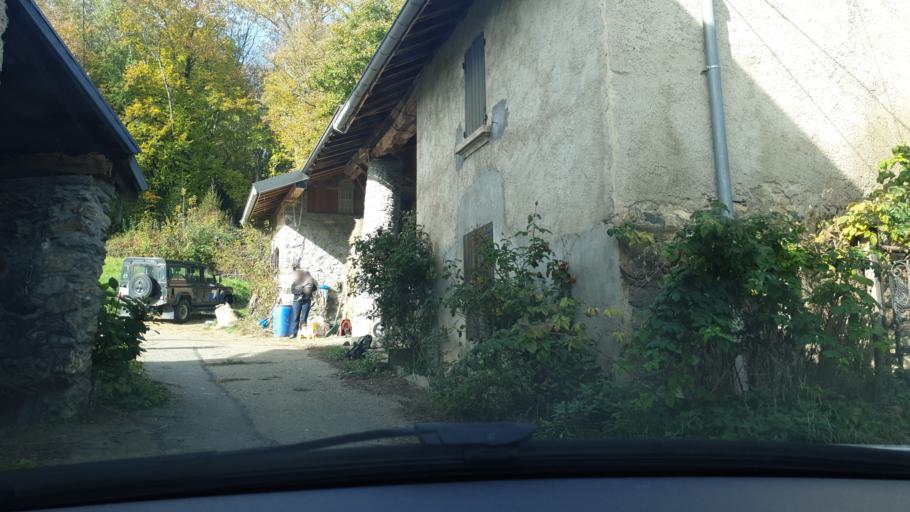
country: FR
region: Rhone-Alpes
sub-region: Departement de la Savoie
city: Aiton
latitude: 45.5029
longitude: 6.2292
